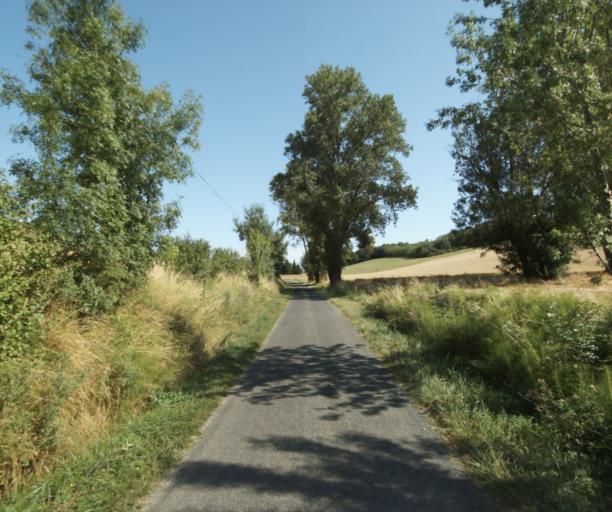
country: FR
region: Midi-Pyrenees
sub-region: Departement de la Haute-Garonne
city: Saint-Felix-Lauragais
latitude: 43.4324
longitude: 1.8477
